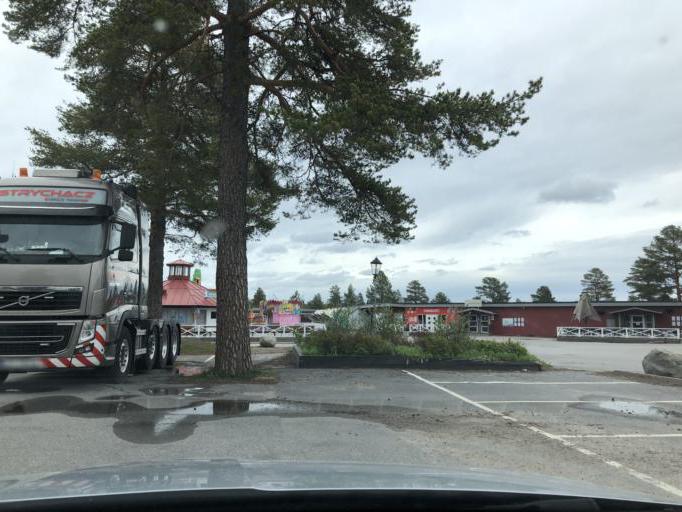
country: SE
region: Norrbotten
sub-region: Pitea Kommun
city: Pitea
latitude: 65.2346
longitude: 21.5313
